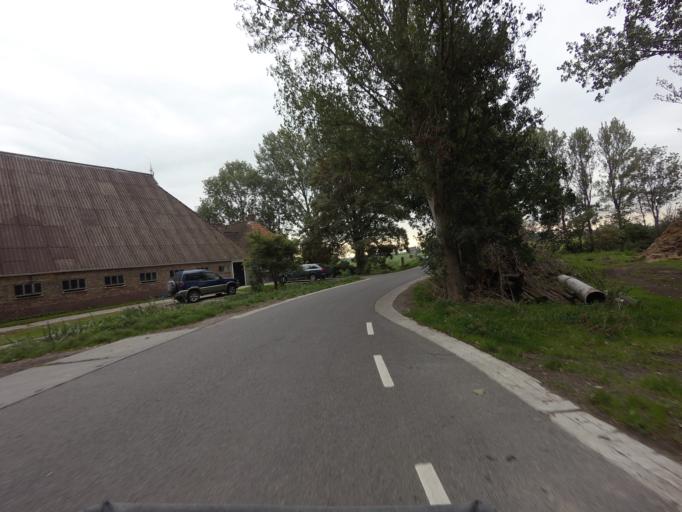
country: NL
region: Friesland
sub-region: Sudwest Fryslan
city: IJlst
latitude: 53.0100
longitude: 5.5856
